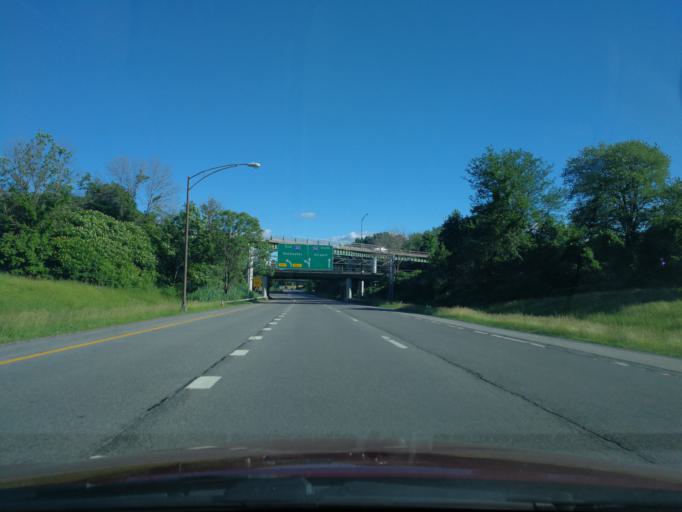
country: US
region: New York
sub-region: Monroe County
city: North Gates
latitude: 43.1595
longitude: -77.6826
